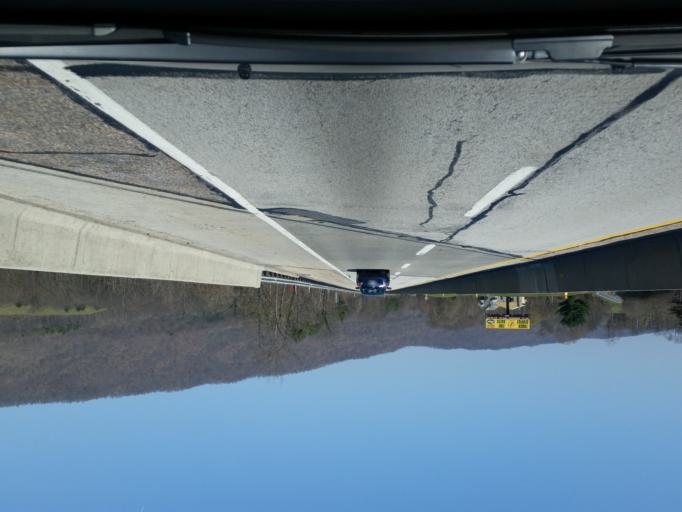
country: US
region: Pennsylvania
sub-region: Franklin County
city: Doylestown
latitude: 40.1589
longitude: -77.6979
